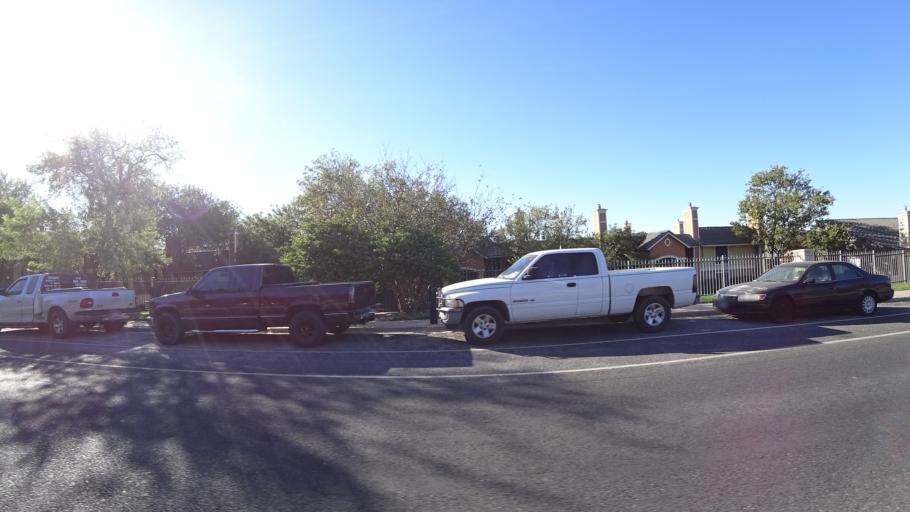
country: US
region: Texas
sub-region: Travis County
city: Austin
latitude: 30.2335
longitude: -97.7285
